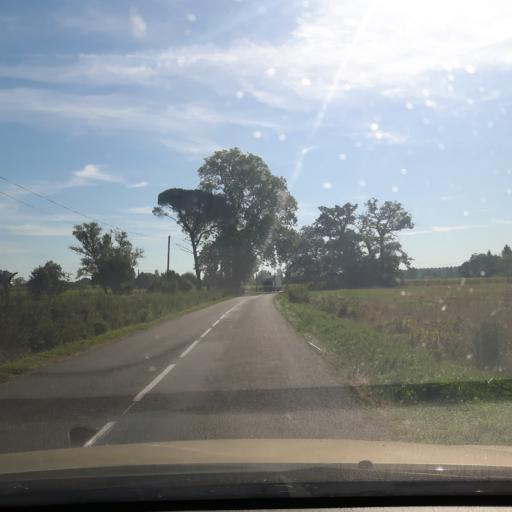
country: FR
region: Midi-Pyrenees
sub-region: Departement de la Haute-Garonne
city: Cepet
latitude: 43.7581
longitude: 1.4345
